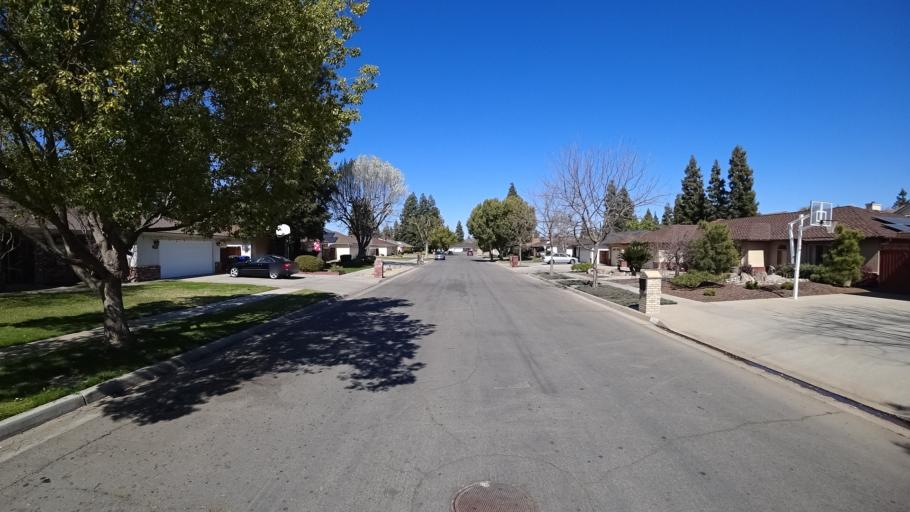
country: US
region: California
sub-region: Fresno County
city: Clovis
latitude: 36.8460
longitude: -119.7499
